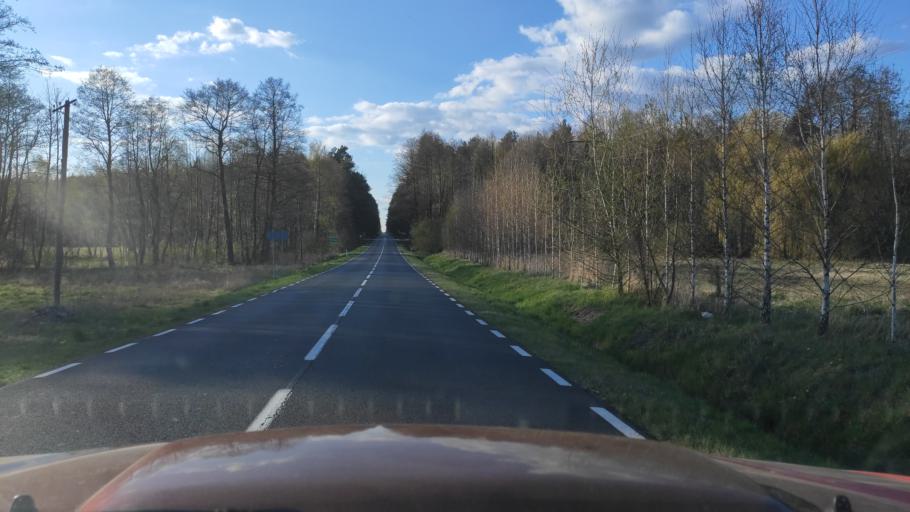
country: PL
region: Masovian Voivodeship
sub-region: Powiat zwolenski
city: Zwolen
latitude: 51.3857
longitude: 21.5547
